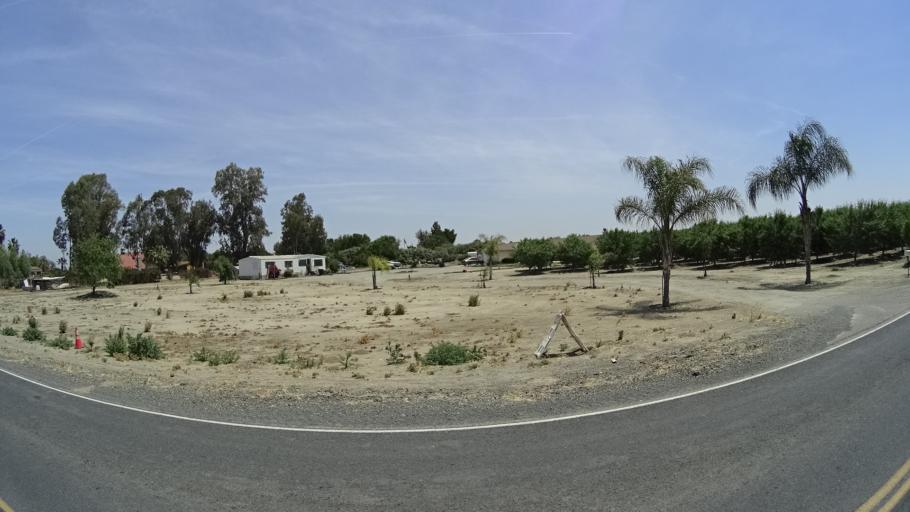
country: US
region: California
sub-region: Fresno County
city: Riverdale
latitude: 36.4009
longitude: -119.8514
